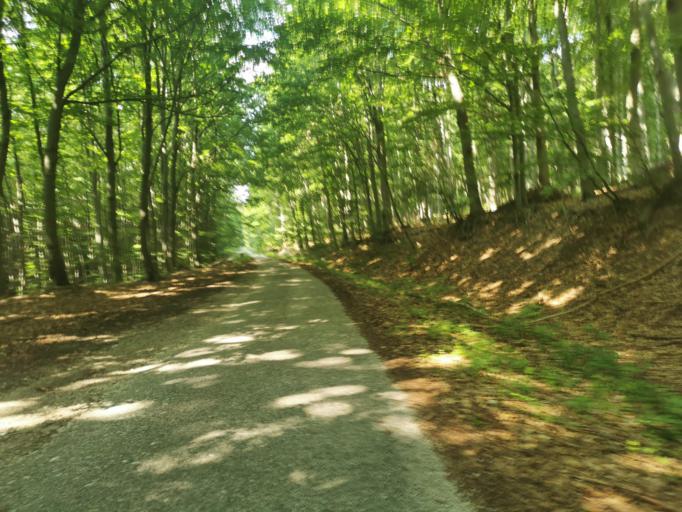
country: SK
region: Trenciansky
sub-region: Okres Myjava
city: Myjava
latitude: 48.8154
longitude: 17.5653
